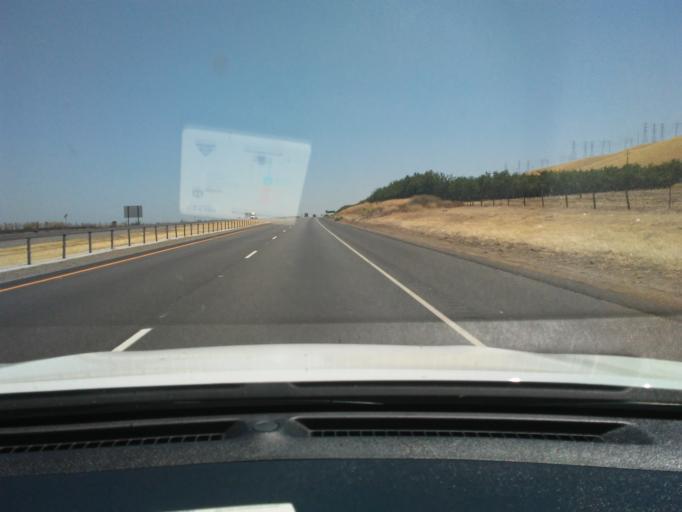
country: US
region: California
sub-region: Stanislaus County
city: Patterson
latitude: 37.5333
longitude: -121.2593
